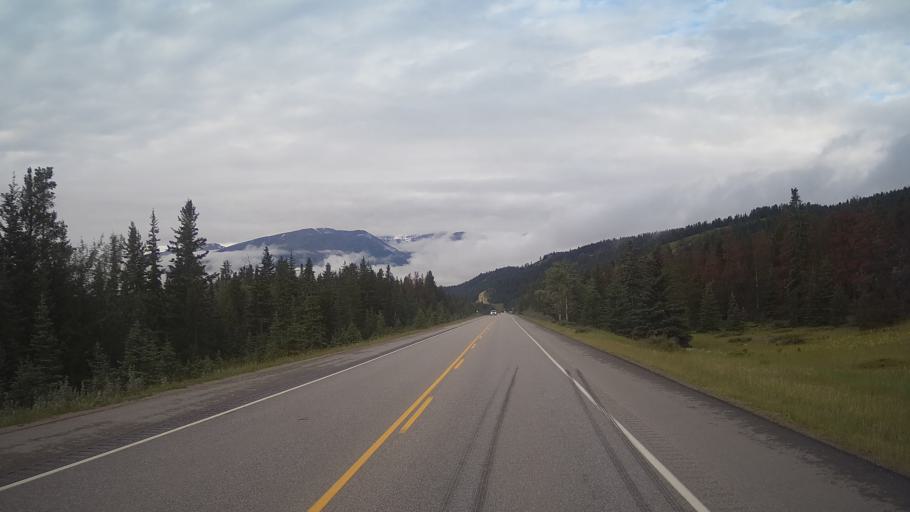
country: CA
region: Alberta
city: Jasper Park Lodge
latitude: 52.9268
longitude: -118.0398
